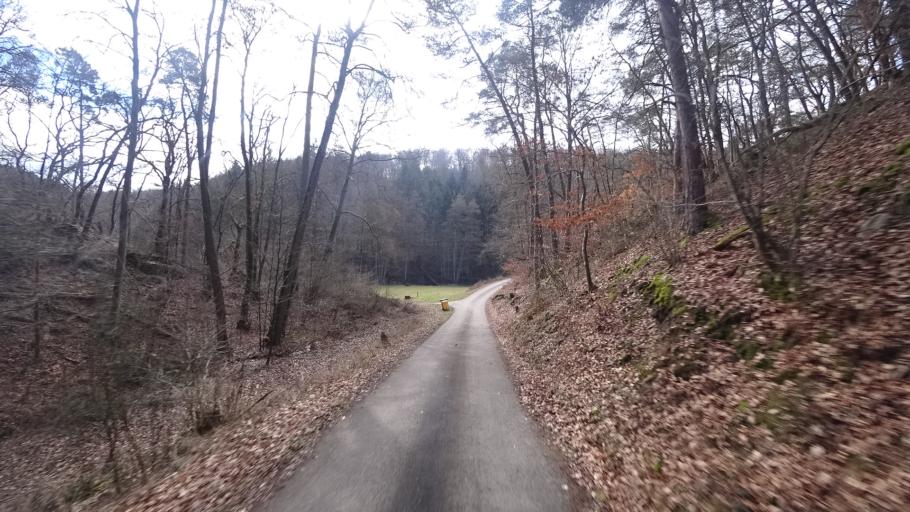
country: DE
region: Rheinland-Pfalz
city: Reichenberg
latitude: 50.1419
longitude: 7.7557
